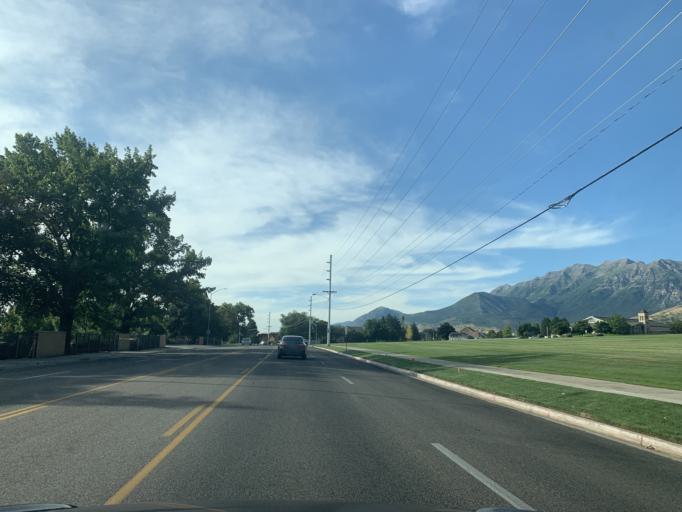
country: US
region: Utah
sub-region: Utah County
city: Provo
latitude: 40.2610
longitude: -111.6442
